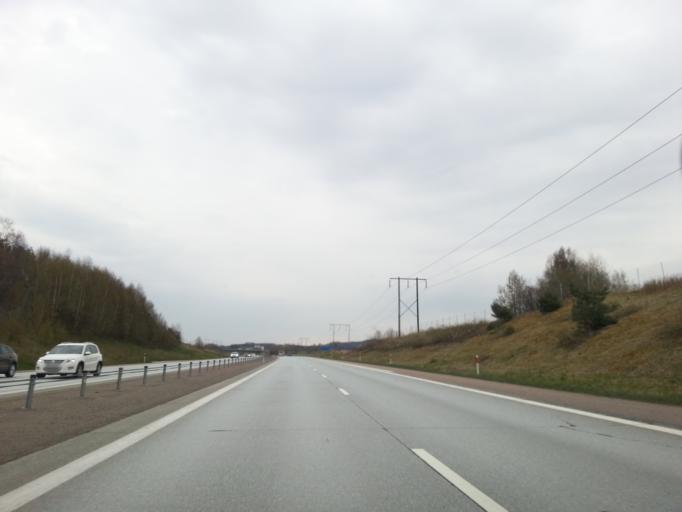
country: SE
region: Halland
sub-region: Halmstads Kommun
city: Getinge
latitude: 56.8559
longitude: 12.6707
